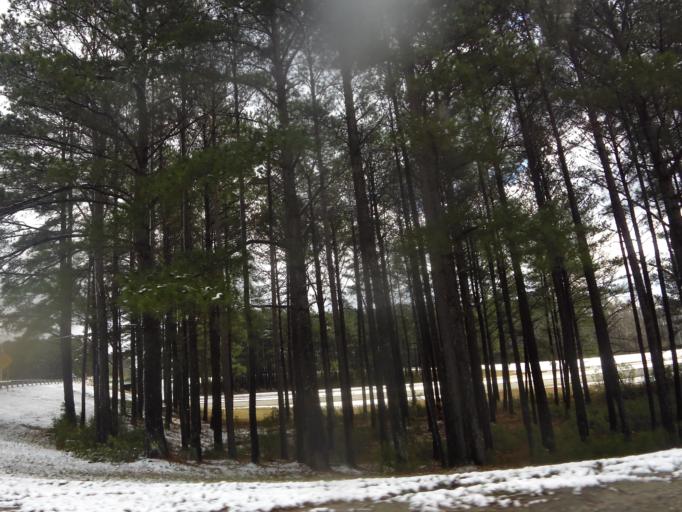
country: US
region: North Carolina
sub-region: Wilson County
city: Lucama
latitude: 35.7022
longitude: -78.0478
